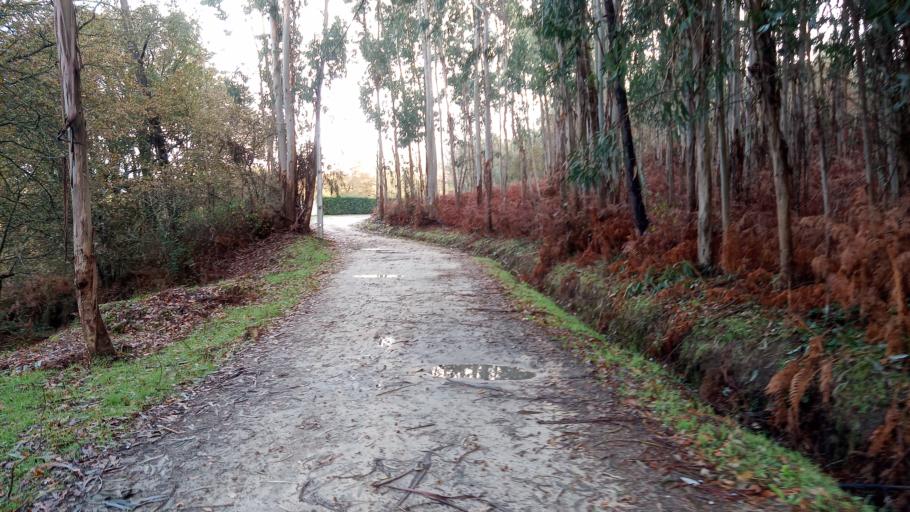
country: PT
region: Viana do Castelo
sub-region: Paredes de Coura
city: Paredes de Coura
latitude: 41.8923
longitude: -8.6147
